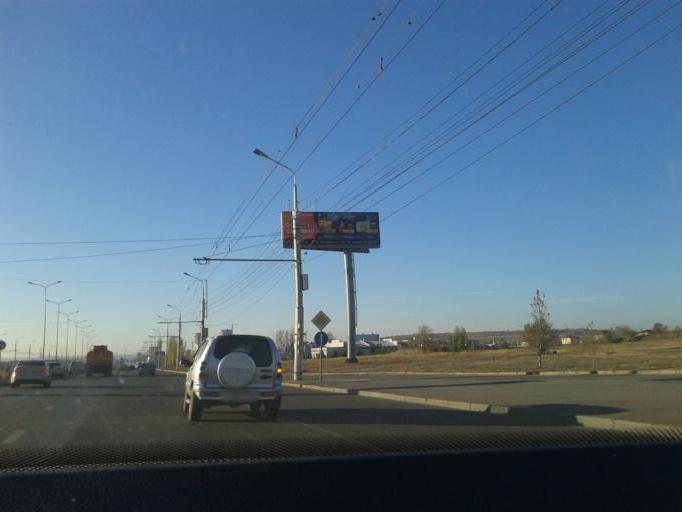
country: RU
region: Volgograd
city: Volgograd
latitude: 48.6400
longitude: 44.4314
